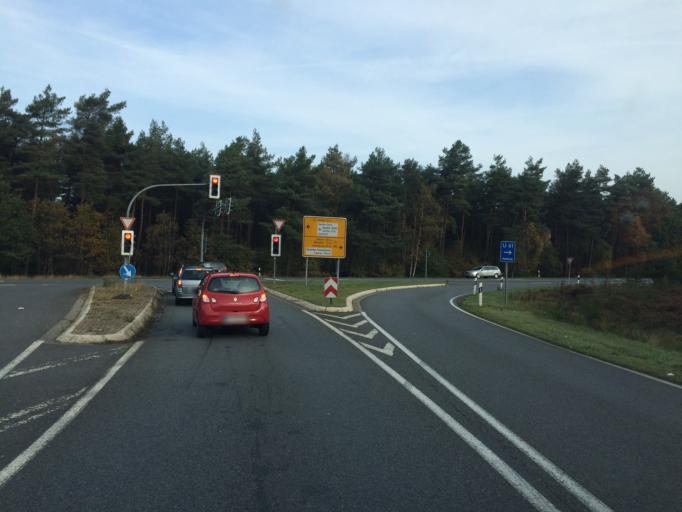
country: DE
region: Lower Saxony
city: Soltau
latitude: 53.0004
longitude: 9.9334
